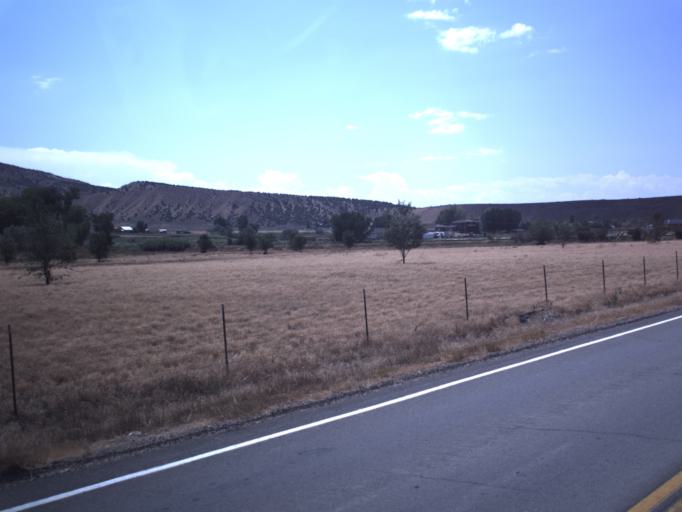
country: US
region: Utah
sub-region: Uintah County
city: Maeser
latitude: 40.4627
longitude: -109.5979
